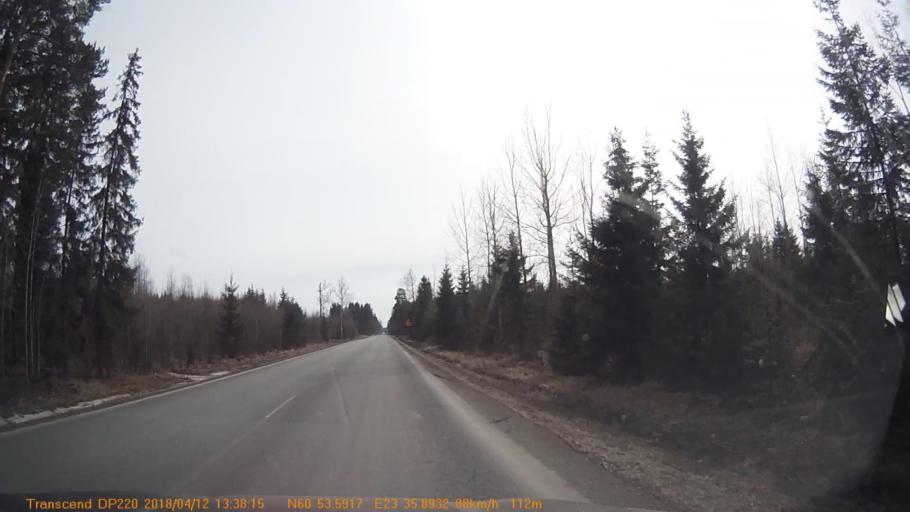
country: FI
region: Haeme
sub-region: Forssa
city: Forssa
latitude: 60.8930
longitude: 23.5983
